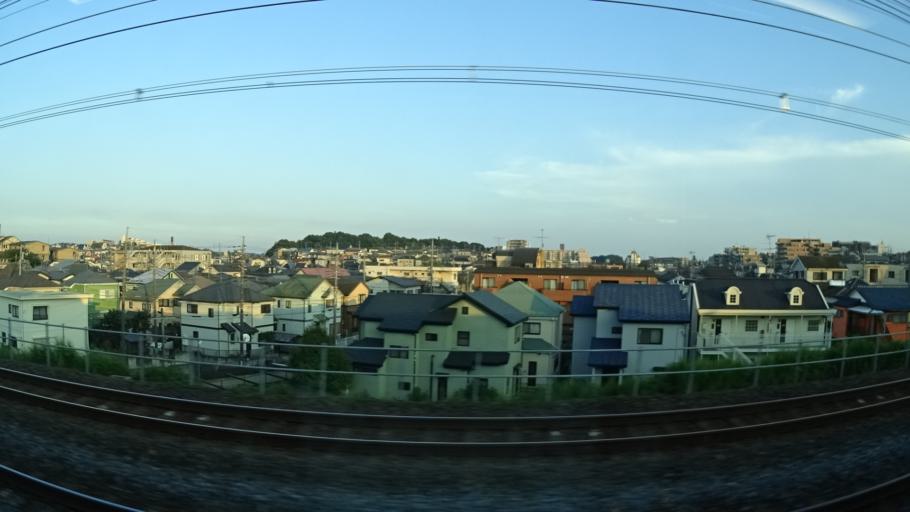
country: JP
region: Chiba
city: Kashiwa
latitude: 35.8360
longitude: 139.9363
